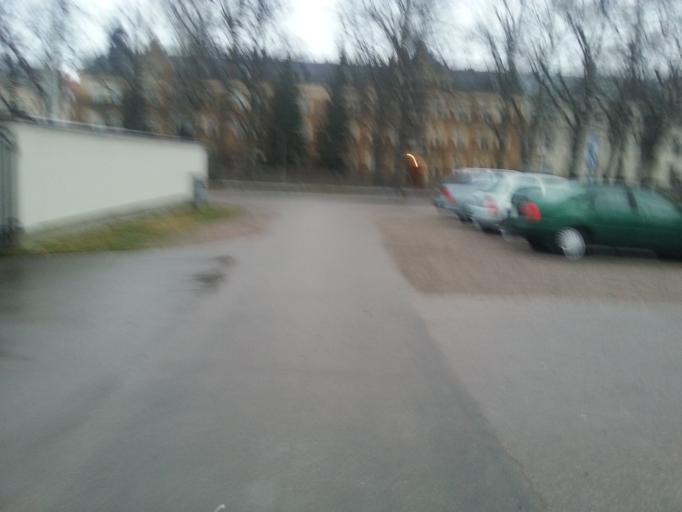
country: SE
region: OEstergoetland
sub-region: Norrkopings Kommun
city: Norrkoping
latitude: 58.5846
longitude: 16.1954
